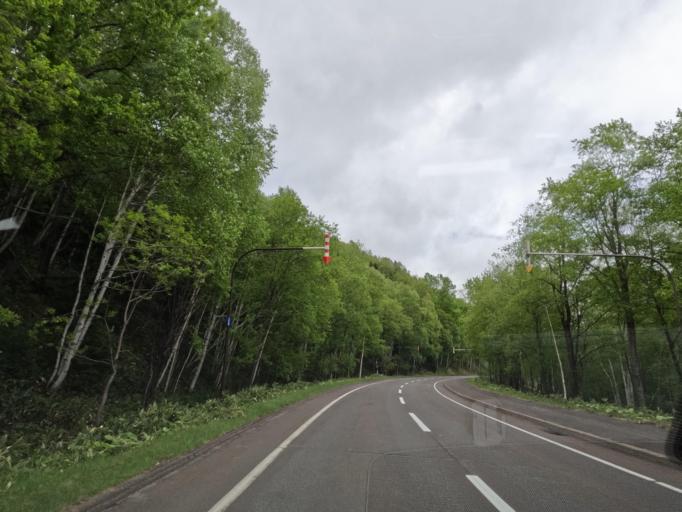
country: JP
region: Hokkaido
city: Kamikawa
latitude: 43.6460
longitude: 143.0212
